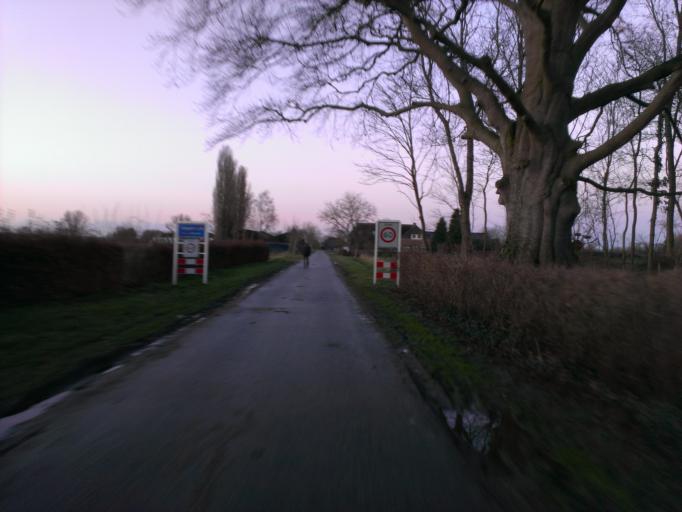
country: NL
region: Gelderland
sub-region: Gemeente Heerde
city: Heerde
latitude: 52.3785
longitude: 6.0850
